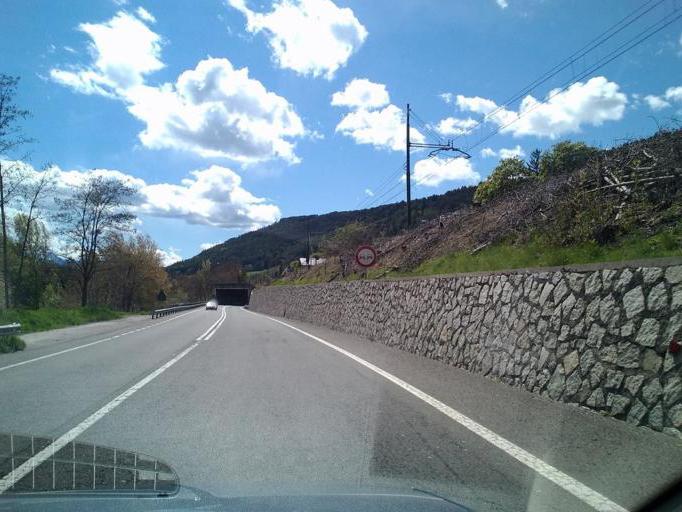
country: IT
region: Trentino-Alto Adige
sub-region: Bolzano
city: Rio di Pusteria
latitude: 46.7992
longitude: 11.6715
